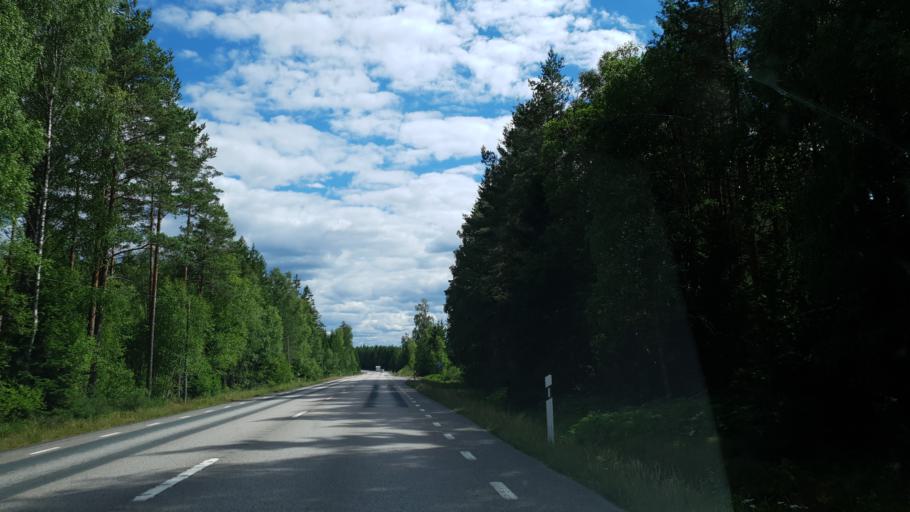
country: SE
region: Kronoberg
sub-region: Uppvidinge Kommun
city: Lenhovda
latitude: 56.8839
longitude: 15.3765
